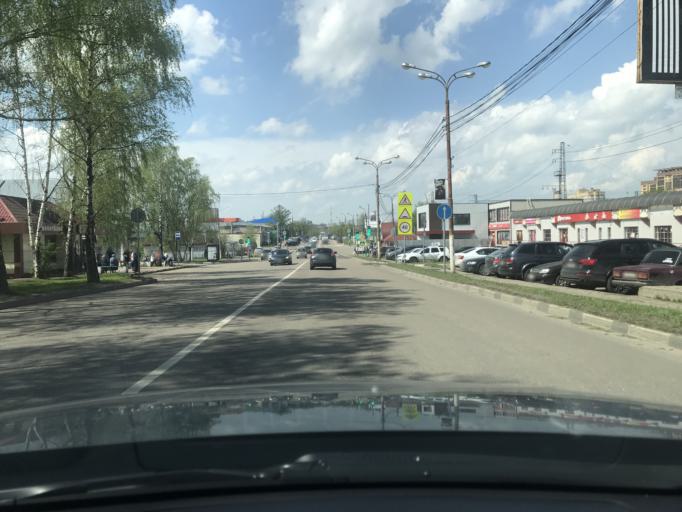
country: RU
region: Moskovskaya
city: Naro-Fominsk
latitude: 55.3824
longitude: 36.7526
